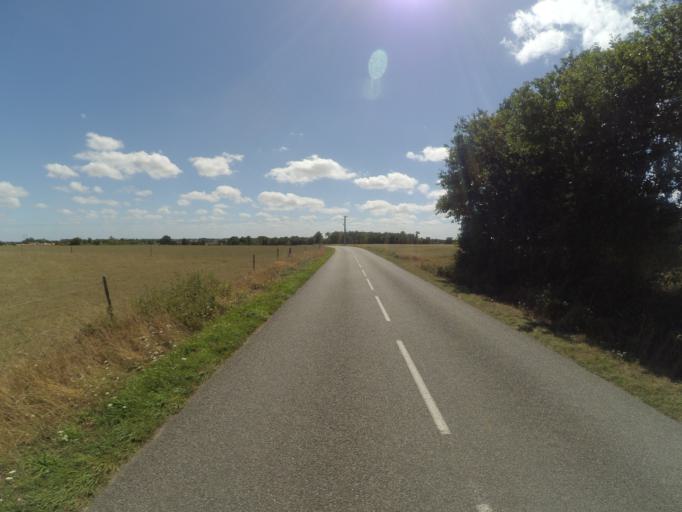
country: FR
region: Pays de la Loire
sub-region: Departement de la Loire-Atlantique
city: La Planche
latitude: 47.0170
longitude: -1.4234
